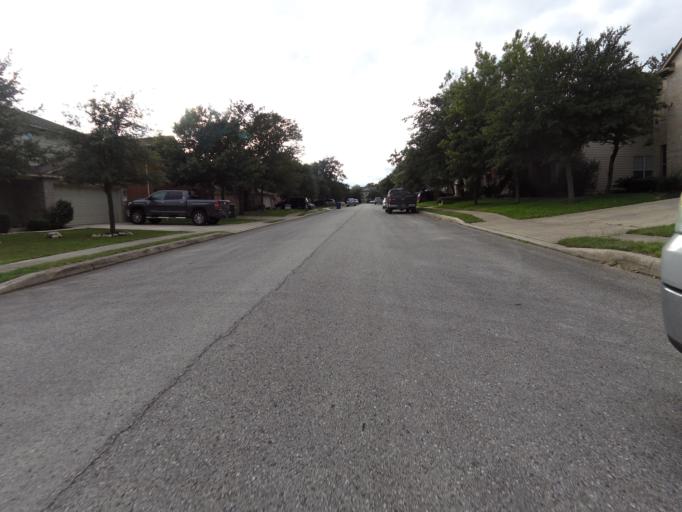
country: US
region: Texas
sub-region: Bexar County
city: Cross Mountain
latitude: 29.6723
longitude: -98.6387
